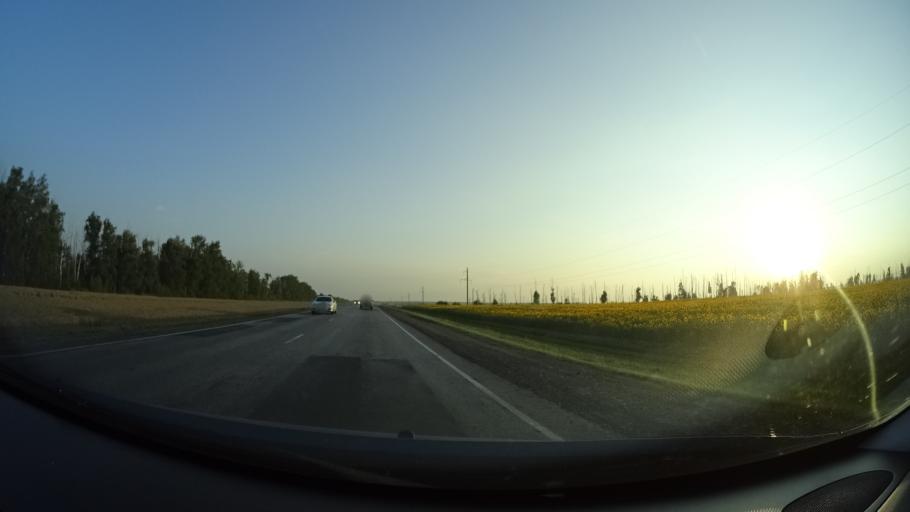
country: RU
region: Samara
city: Sernovodsk
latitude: 53.9490
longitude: 51.3728
